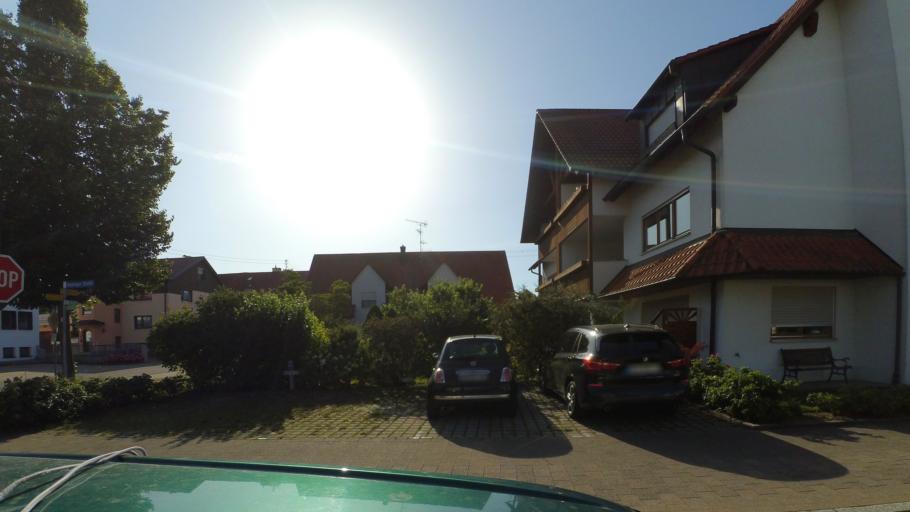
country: DE
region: Bavaria
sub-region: Swabia
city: Bachingen an der Brenz
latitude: 48.5487
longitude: 10.3104
